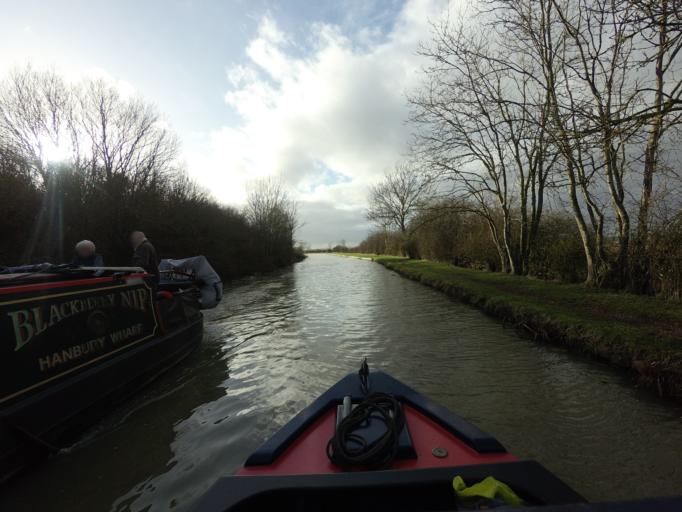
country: GB
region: England
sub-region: Warwickshire
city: Dunchurch
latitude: 52.2821
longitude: -1.2461
